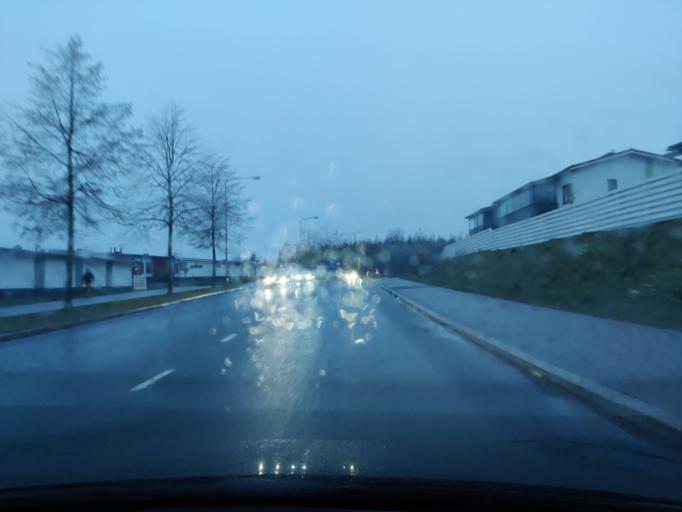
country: FI
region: Northern Savo
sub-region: Kuopio
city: Kuopio
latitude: 62.8285
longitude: 27.6758
